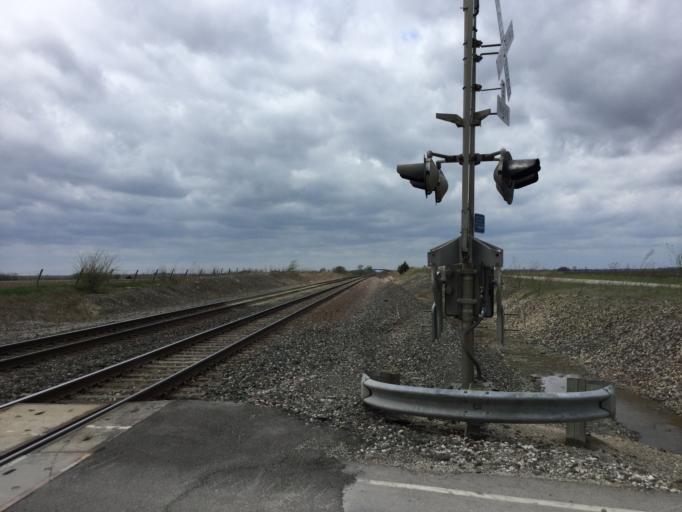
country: US
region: Kansas
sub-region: Osage County
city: Osage City
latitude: 38.4094
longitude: -95.8762
